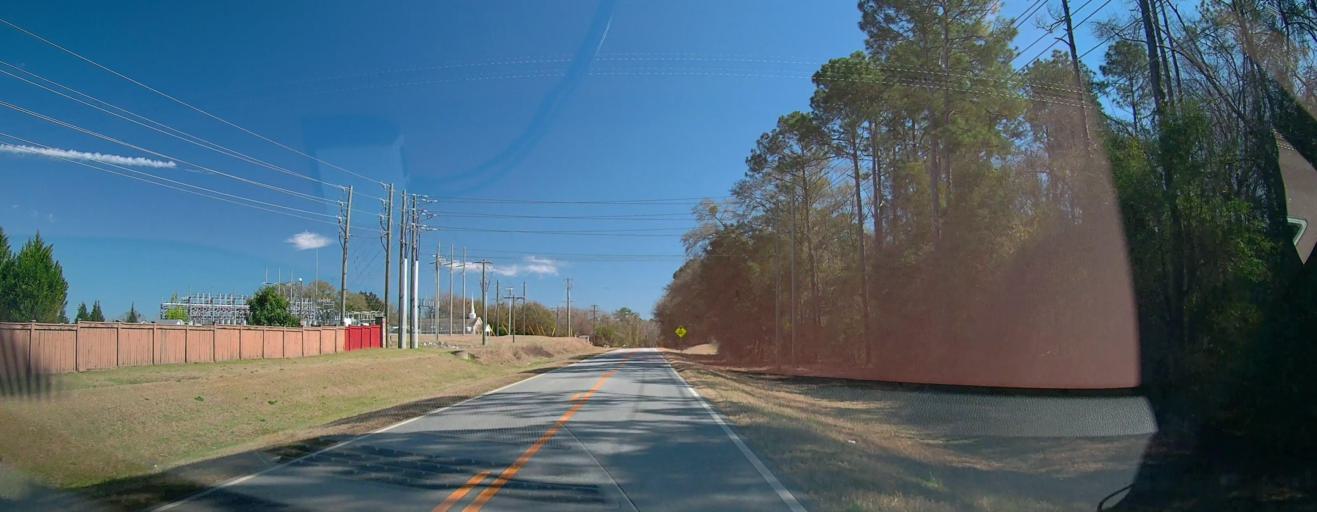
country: US
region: Georgia
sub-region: Houston County
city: Perry
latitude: 32.4937
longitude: -83.6591
